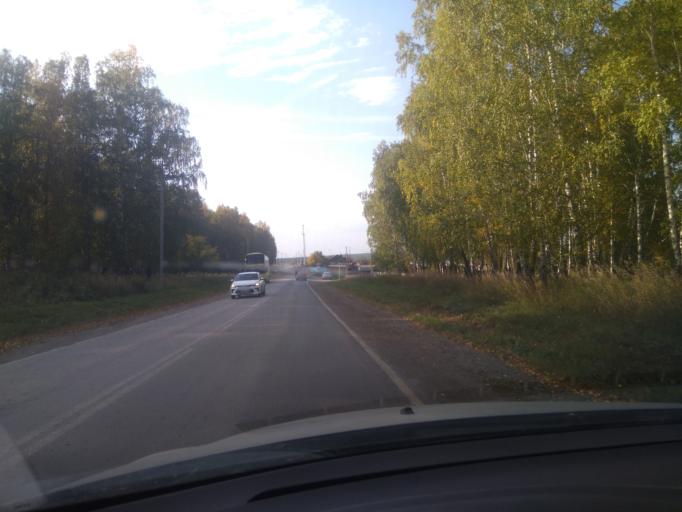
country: RU
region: Sverdlovsk
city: Pokrovskoye
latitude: 56.4300
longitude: 61.5952
